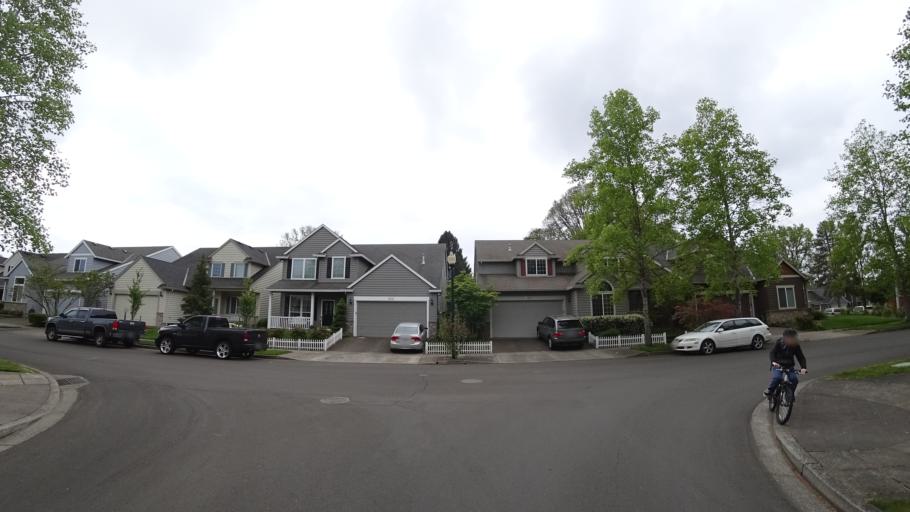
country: US
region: Oregon
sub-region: Washington County
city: Hillsboro
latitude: 45.5433
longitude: -122.9749
